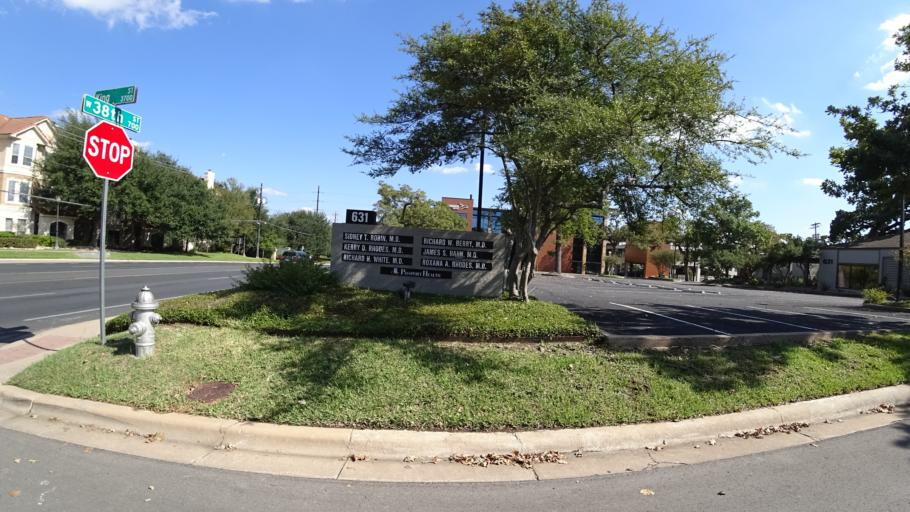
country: US
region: Texas
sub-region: Travis County
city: Austin
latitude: 30.3035
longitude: -97.7398
